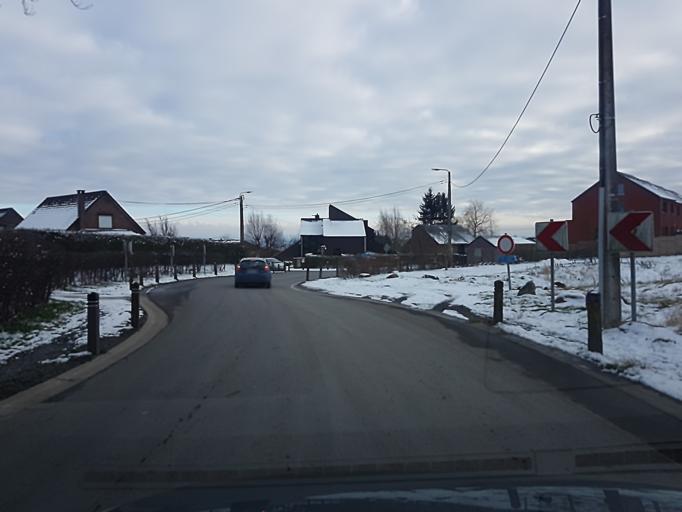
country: BE
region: Wallonia
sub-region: Province de Liege
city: Soumagne
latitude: 50.6304
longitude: 5.7634
